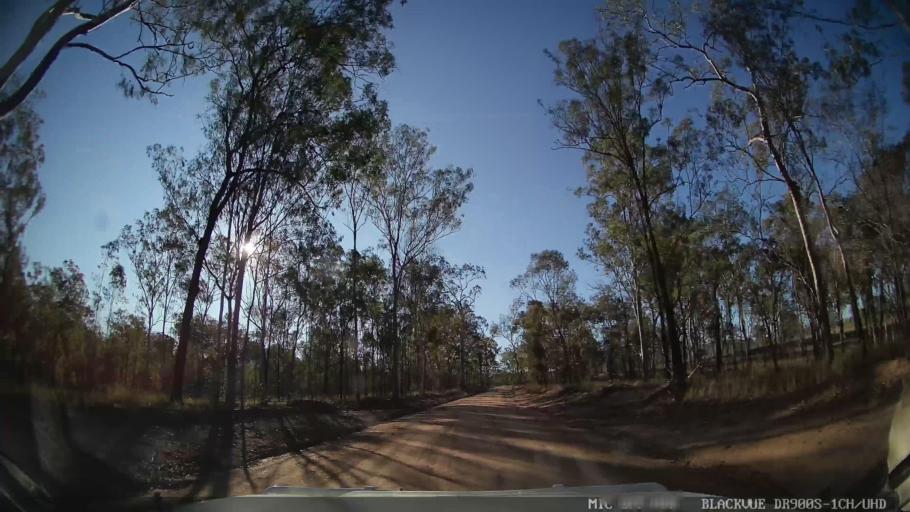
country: AU
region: Queensland
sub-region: Bundaberg
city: Sharon
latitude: -24.7381
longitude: 151.5236
